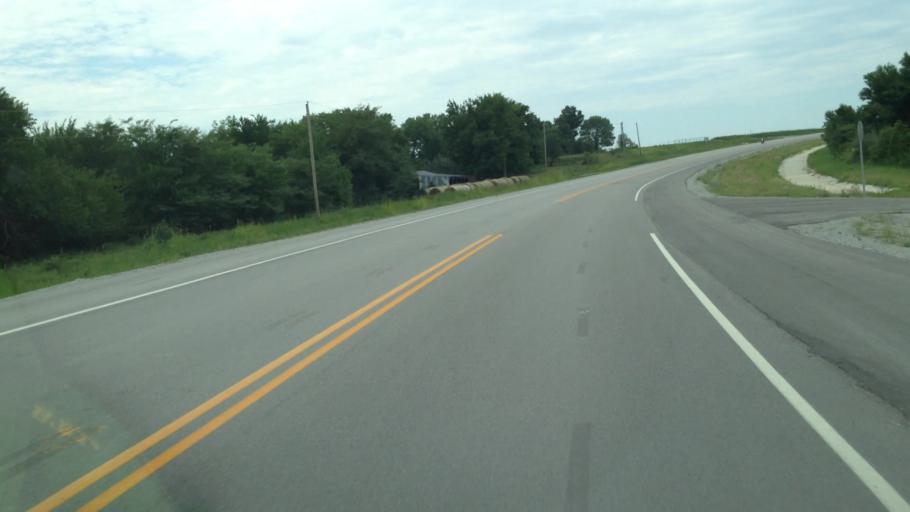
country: US
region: Kansas
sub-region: Labette County
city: Chetopa
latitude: 36.8854
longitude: -95.0989
